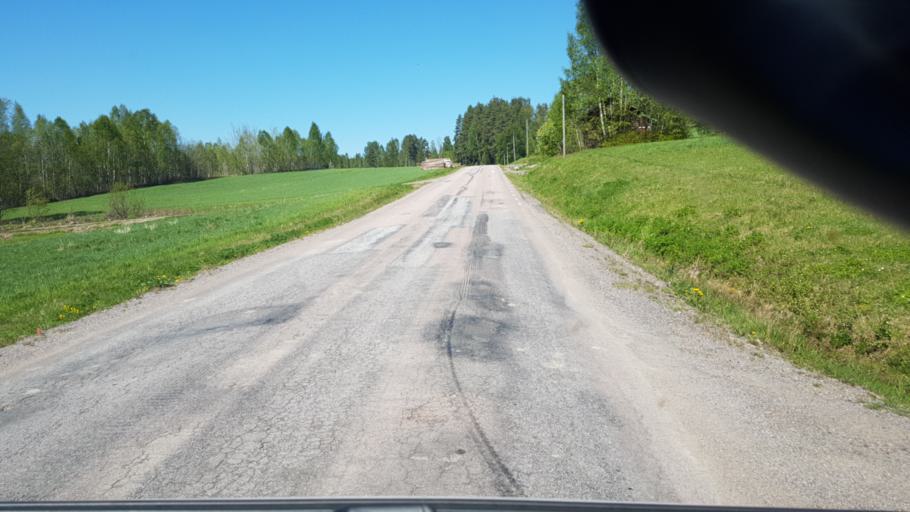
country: SE
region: Vaermland
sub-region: Eda Kommun
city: Amotfors
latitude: 59.9125
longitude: 12.5225
